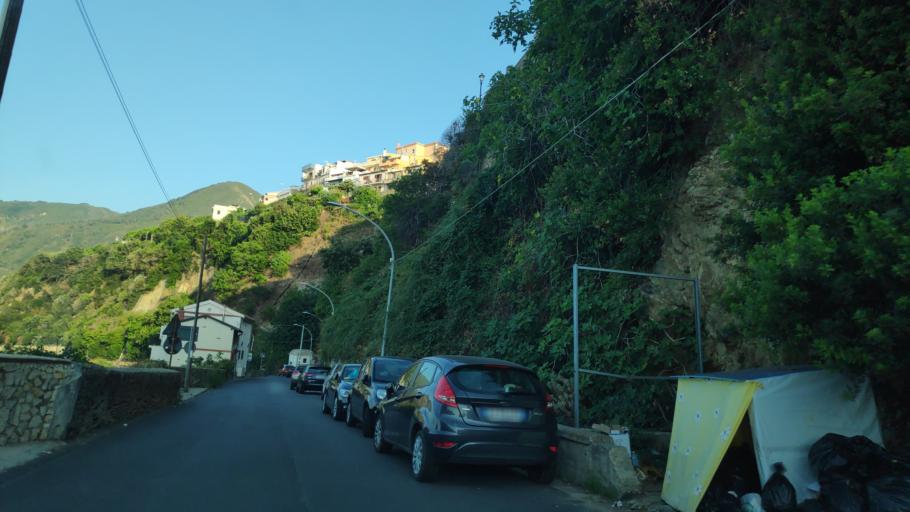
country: IT
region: Calabria
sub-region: Provincia di Reggio Calabria
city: Scilla
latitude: 38.2542
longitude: 15.7166
